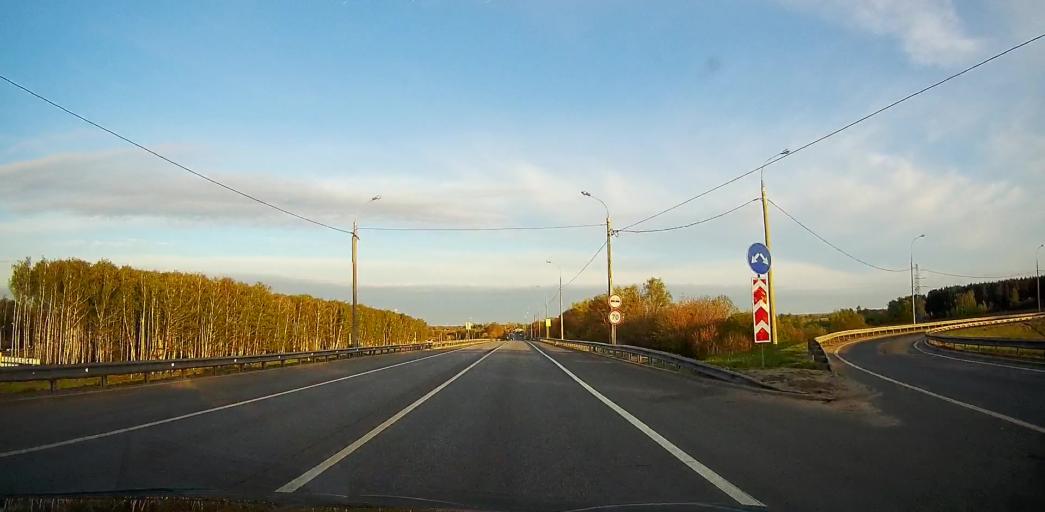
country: RU
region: Moskovskaya
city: Troitskoye
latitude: 55.2344
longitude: 38.5486
